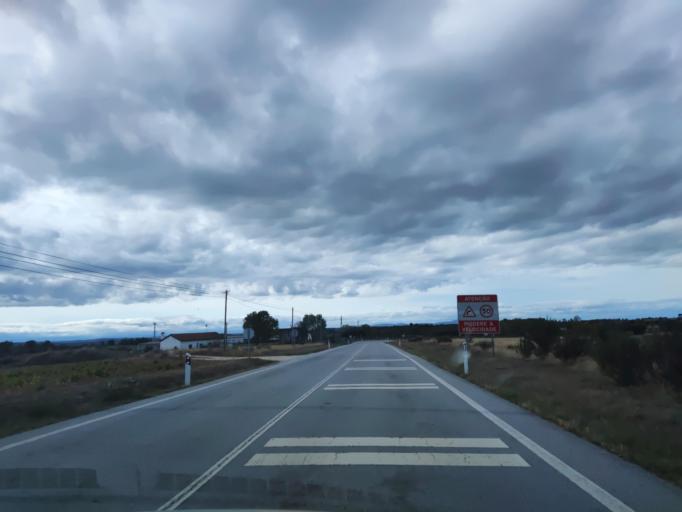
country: ES
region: Castille and Leon
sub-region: Provincia de Salamanca
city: Aldea del Obispo
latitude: 40.6765
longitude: -6.8667
